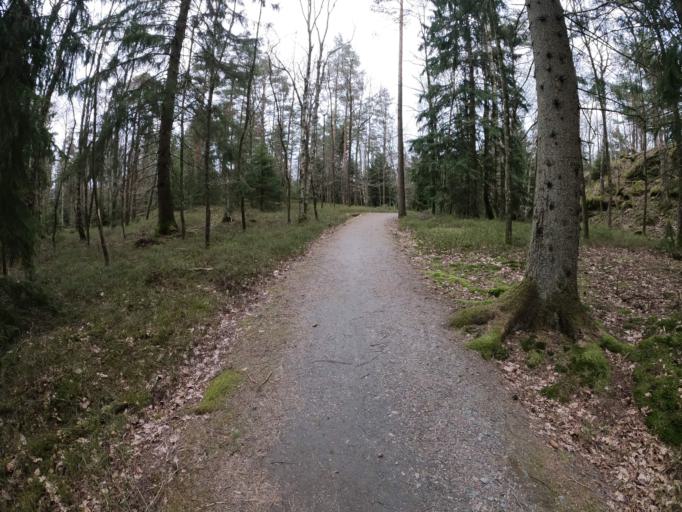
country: SE
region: Vaestra Goetaland
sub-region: Harryda Kommun
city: Molnlycke
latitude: 57.6215
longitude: 12.1054
